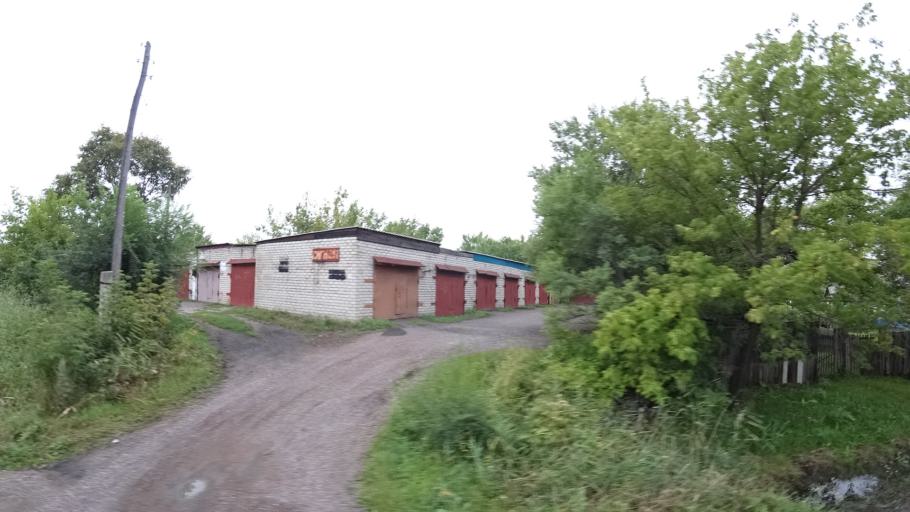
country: RU
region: Primorskiy
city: Chernigovka
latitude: 44.3331
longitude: 132.5321
